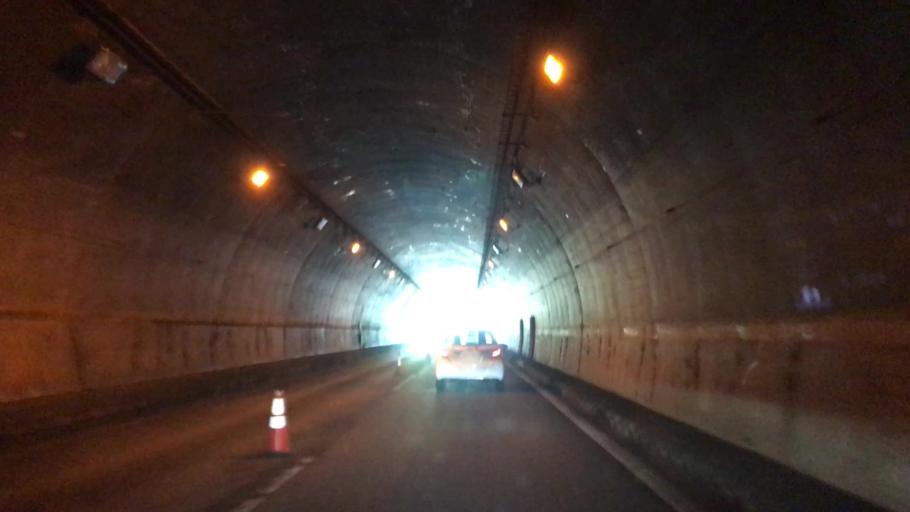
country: JP
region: Hokkaido
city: Otaru
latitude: 43.1681
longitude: 141.0433
